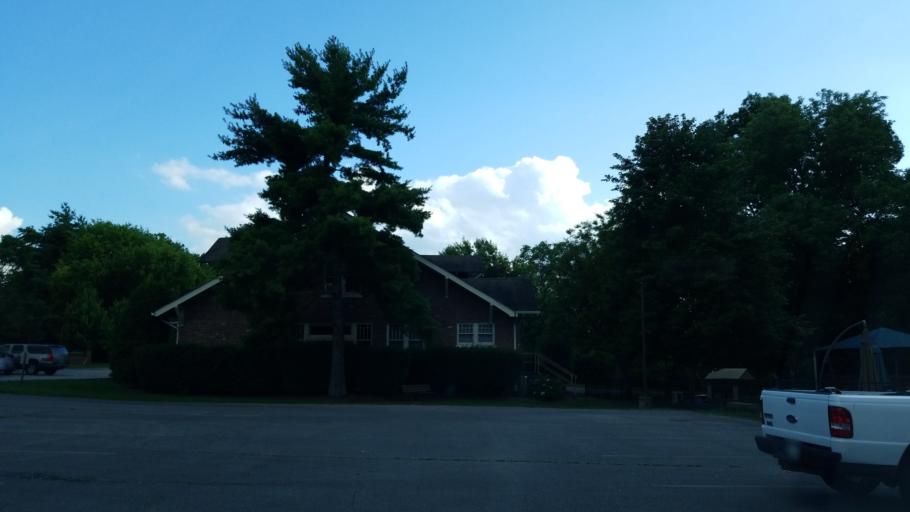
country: US
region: Tennessee
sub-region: Williamson County
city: Brentwood
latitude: 36.0287
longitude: -86.7946
